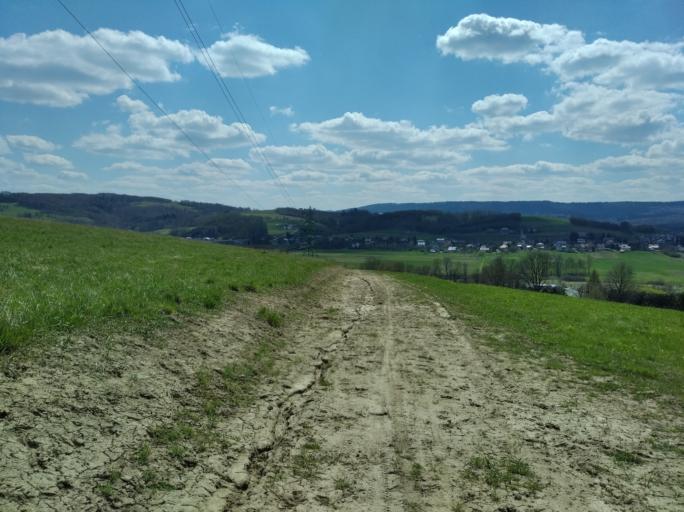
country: PL
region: Subcarpathian Voivodeship
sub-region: Powiat strzyzowski
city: Strzyzow
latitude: 49.8716
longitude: 21.8092
